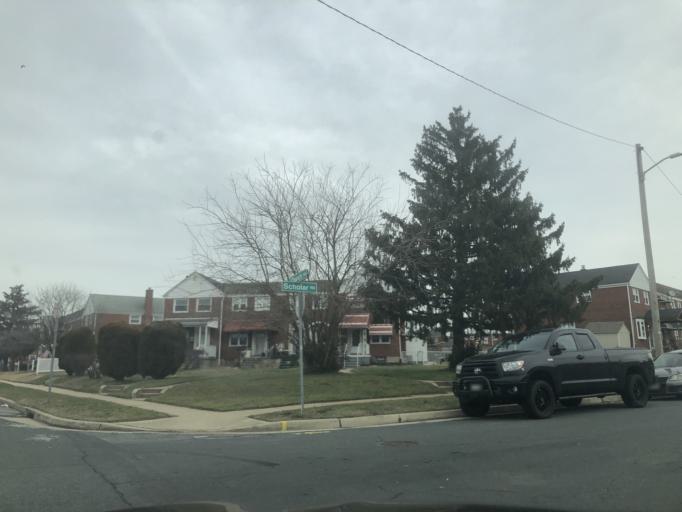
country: US
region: Maryland
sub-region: Baltimore County
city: Dundalk
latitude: 39.2635
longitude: -76.5004
